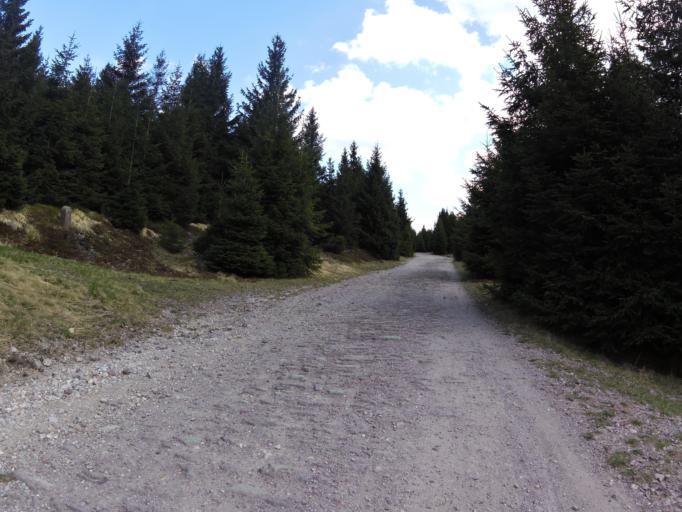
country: DE
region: Thuringia
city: Unterschonau
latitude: 50.7332
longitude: 10.6235
